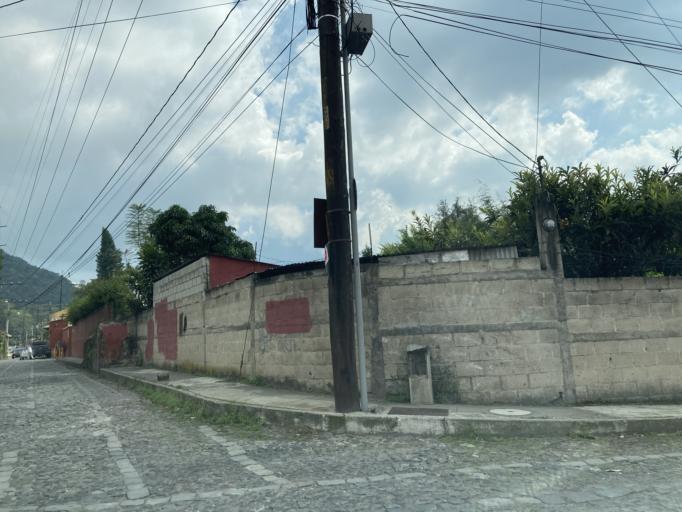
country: GT
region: Sacatepequez
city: Antigua Guatemala
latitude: 14.5615
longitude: -90.7270
